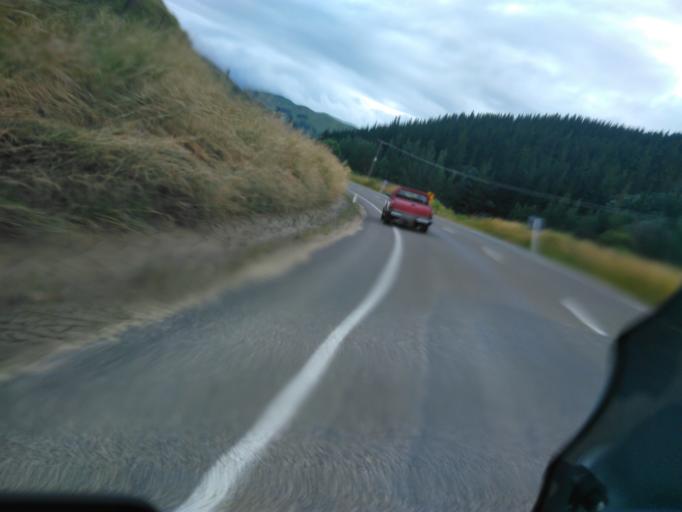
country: NZ
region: Gisborne
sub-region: Gisborne District
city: Gisborne
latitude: -38.4607
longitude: 177.7450
